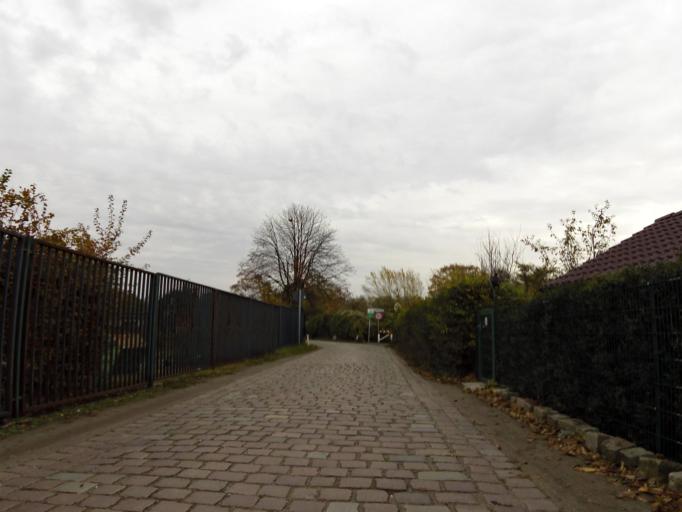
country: DE
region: Berlin
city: Schoneberg Bezirk
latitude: 52.4705
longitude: 13.3593
